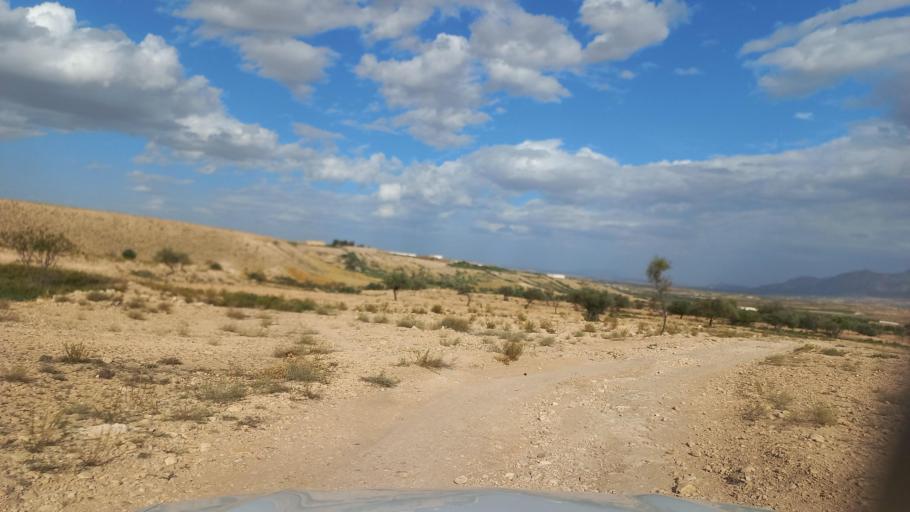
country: TN
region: Al Qasrayn
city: Sbiba
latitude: 35.4506
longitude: 9.0803
